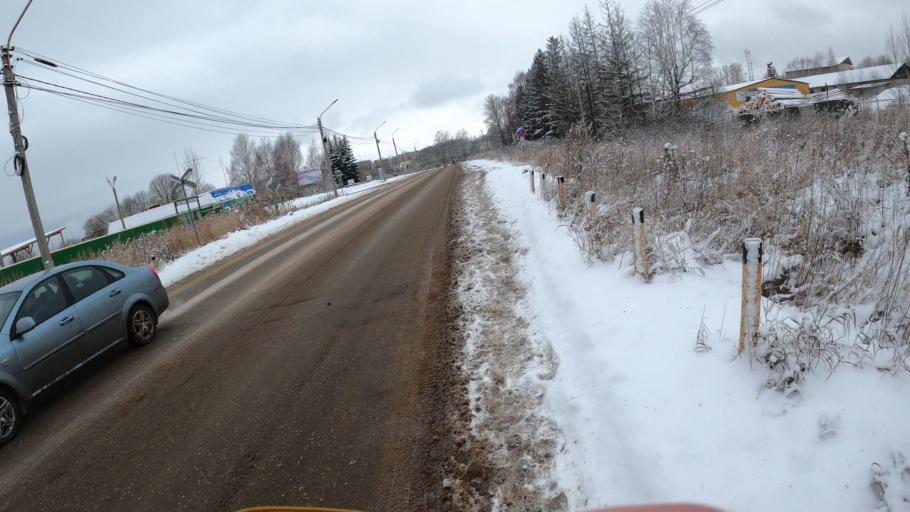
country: RU
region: Jaroslavl
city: Pereslavl'-Zalesskiy
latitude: 56.7380
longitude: 38.9009
